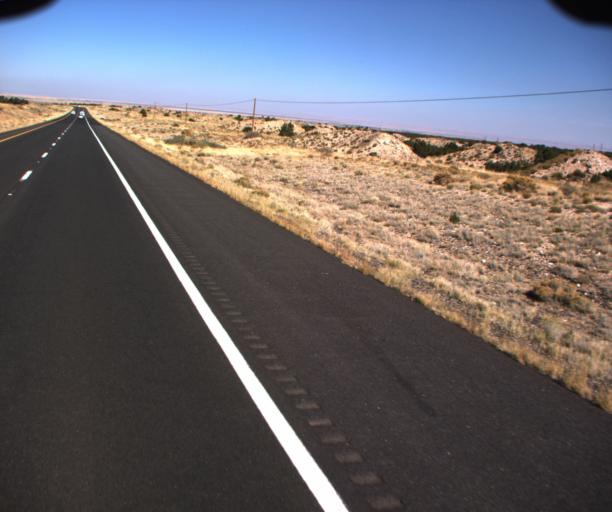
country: US
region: Arizona
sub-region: Coconino County
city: Flagstaff
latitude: 35.5088
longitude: -111.5472
